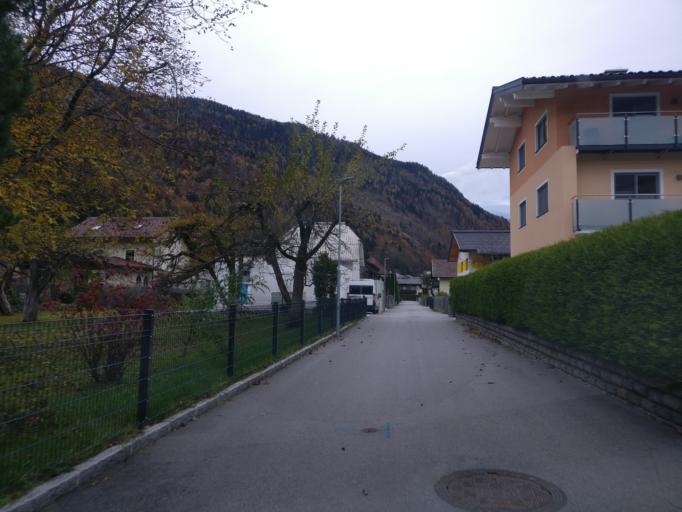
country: AT
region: Salzburg
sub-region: Politischer Bezirk Sankt Johann im Pongau
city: Bischofshofen
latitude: 47.4260
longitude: 13.2195
